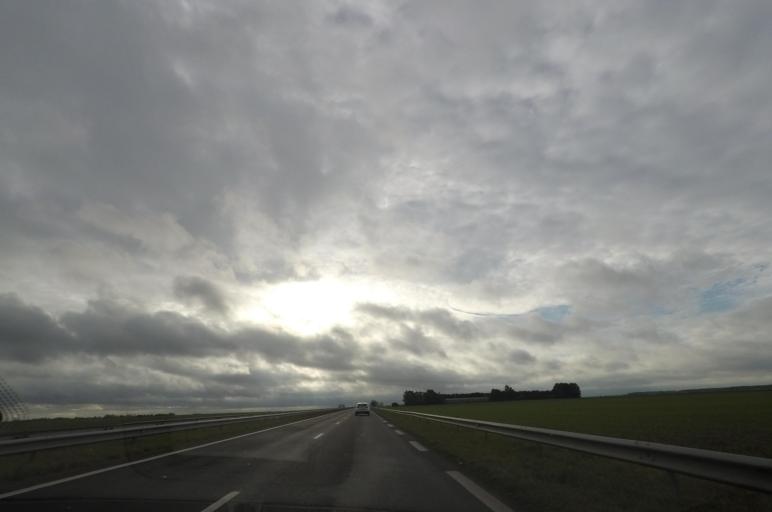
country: FR
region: Centre
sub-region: Departement du Loir-et-Cher
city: Vendome
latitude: 47.7275
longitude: 1.1509
